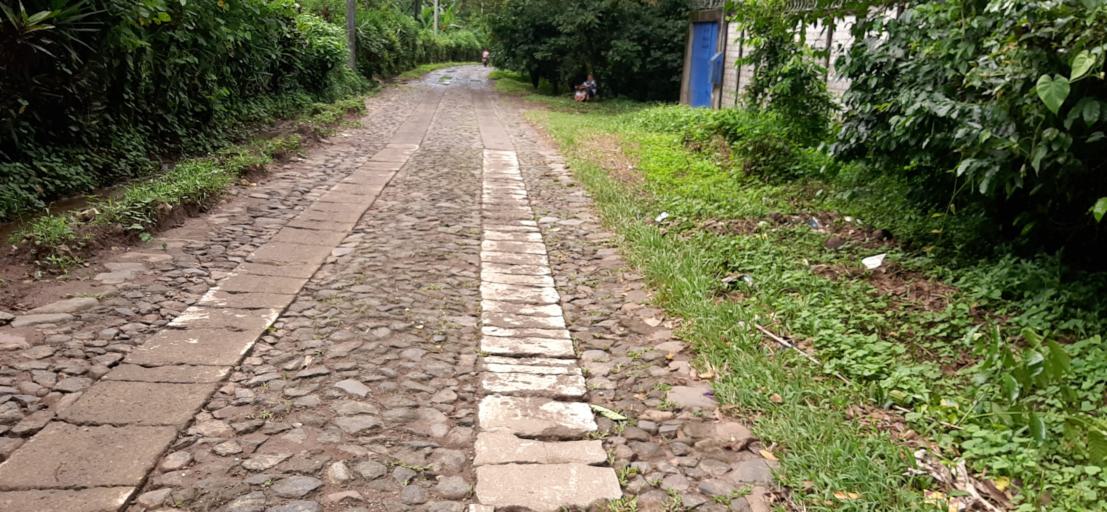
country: GT
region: Retalhuleu
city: San Martin Zapotitlan
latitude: 14.6070
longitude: -91.5749
